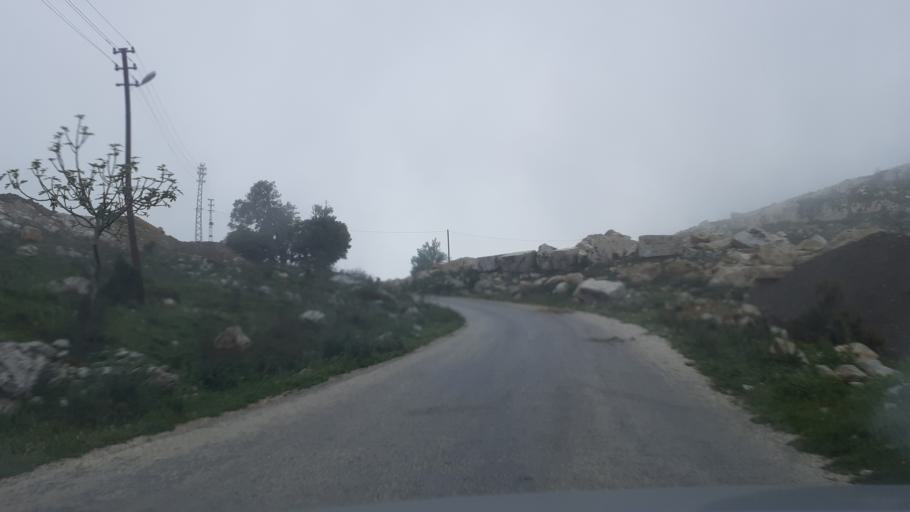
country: TR
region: Hatay
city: Yeditepe
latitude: 35.9685
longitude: 36.0067
